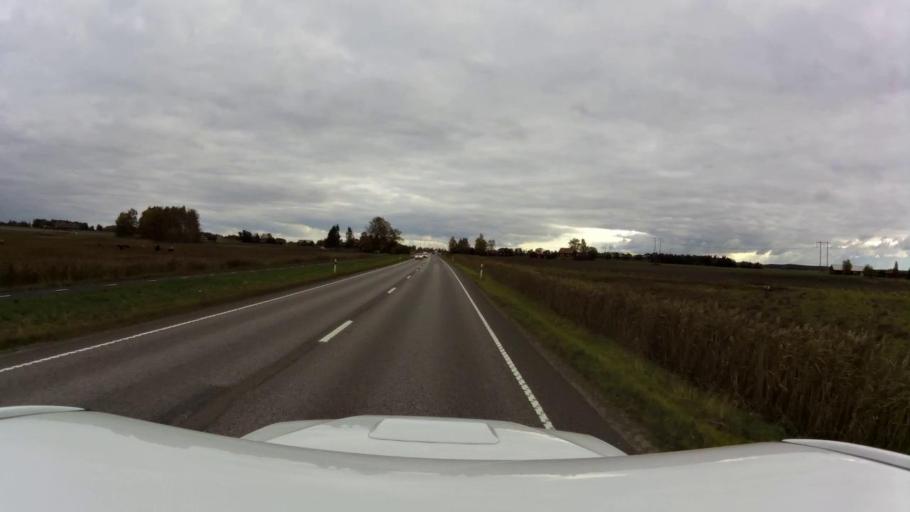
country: SE
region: OEstergoetland
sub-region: Linkopings Kommun
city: Berg
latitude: 58.4534
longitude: 15.5531
